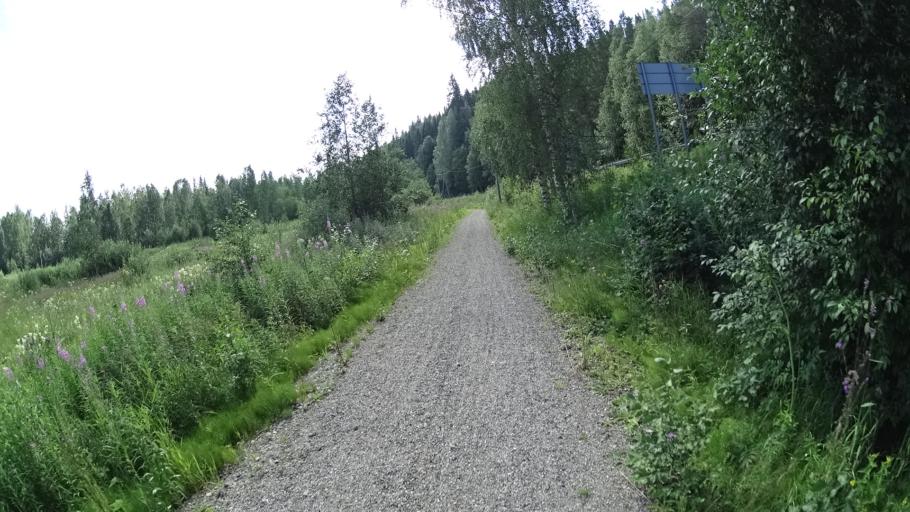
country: FI
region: North Karelia
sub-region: Pielisen Karjala
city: Lieksa
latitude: 63.1180
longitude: 29.7969
